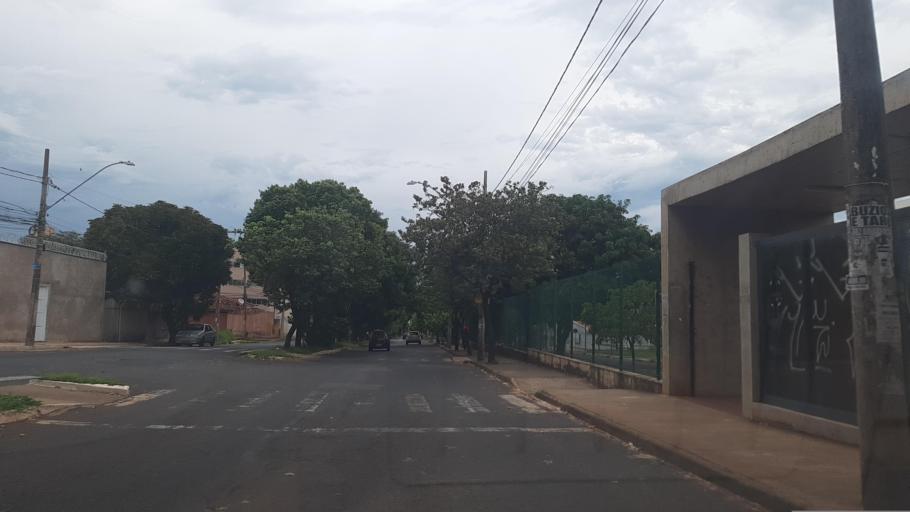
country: BR
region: Minas Gerais
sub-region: Uberlandia
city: Uberlandia
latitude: -18.9198
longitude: -48.2569
